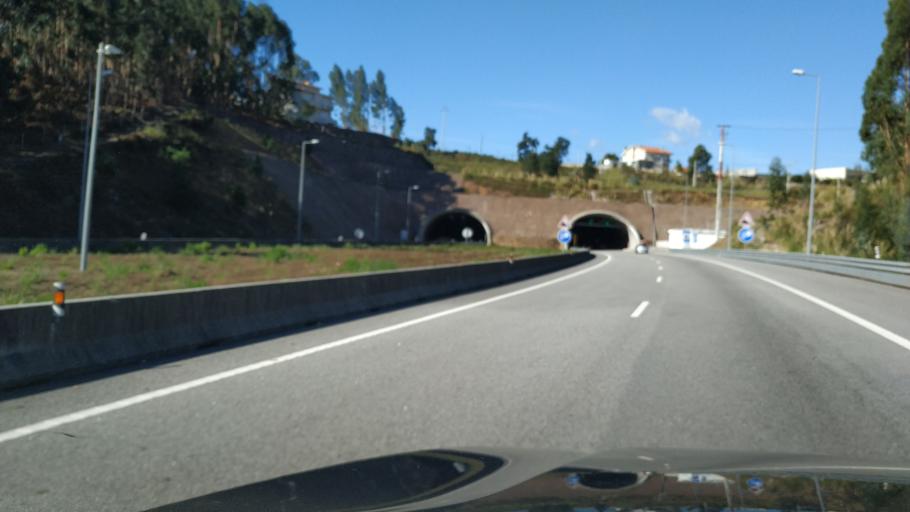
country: PT
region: Porto
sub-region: Vila Nova de Gaia
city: Sandim
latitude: 41.0532
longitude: -8.5132
